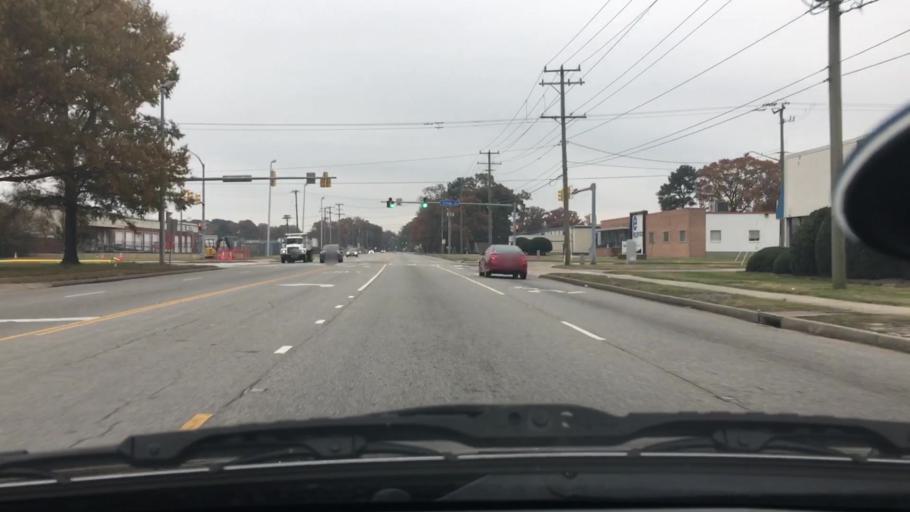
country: US
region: Virginia
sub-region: City of Norfolk
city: Norfolk
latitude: 36.8593
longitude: -76.2426
